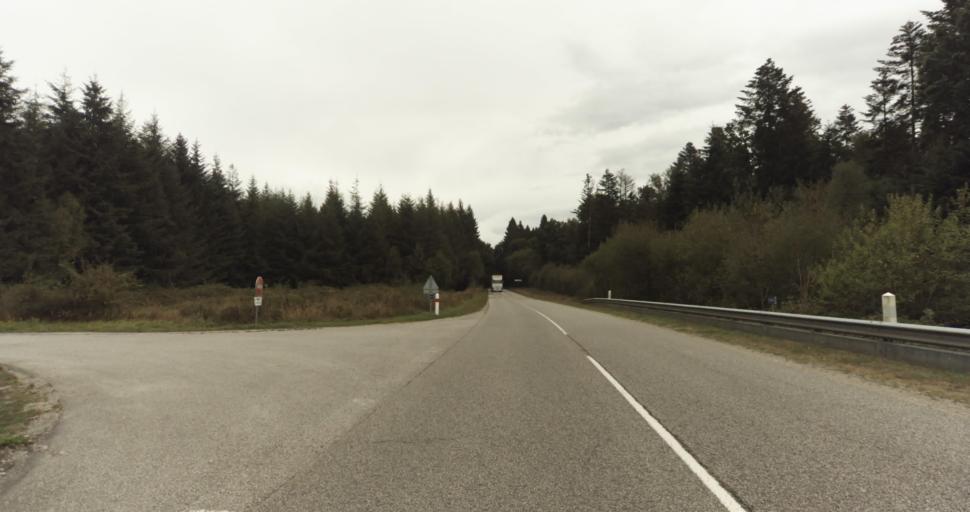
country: FR
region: Lower Normandy
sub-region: Departement de l'Orne
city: Gace
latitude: 48.7957
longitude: 0.3381
